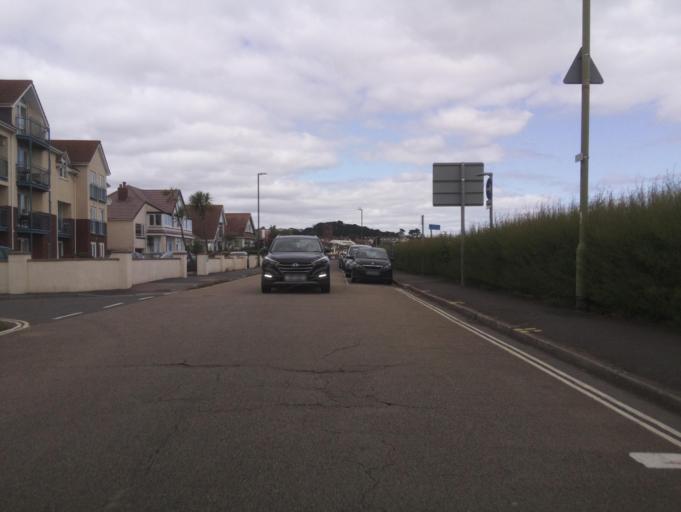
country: GB
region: England
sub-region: Borough of Torbay
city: Paignton
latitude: 50.4429
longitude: -3.5579
